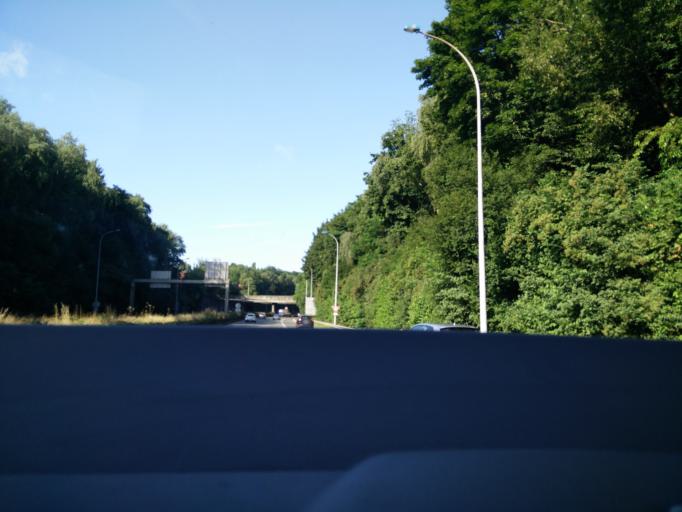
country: FR
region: Nord-Pas-de-Calais
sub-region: Departement du Nord
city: Lambersart
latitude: 50.6557
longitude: 3.0128
